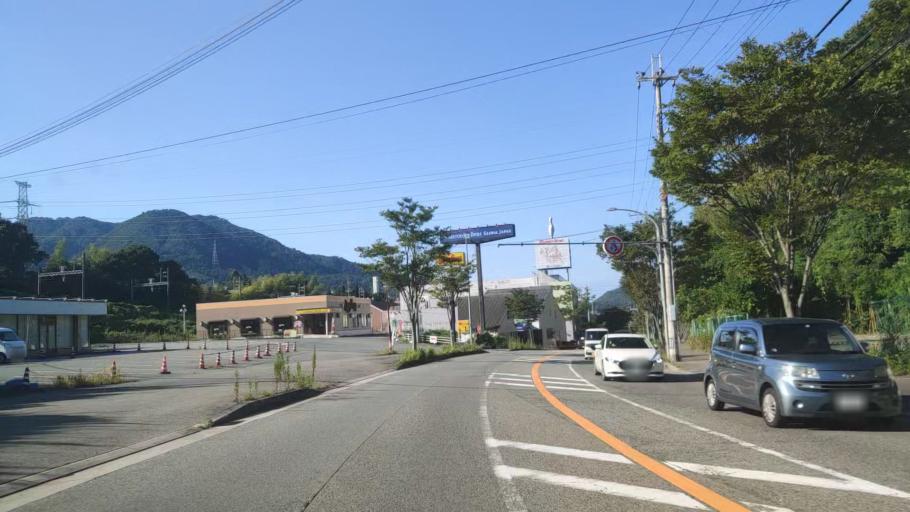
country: JP
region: Hyogo
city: Kobe
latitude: 34.7738
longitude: 135.1937
